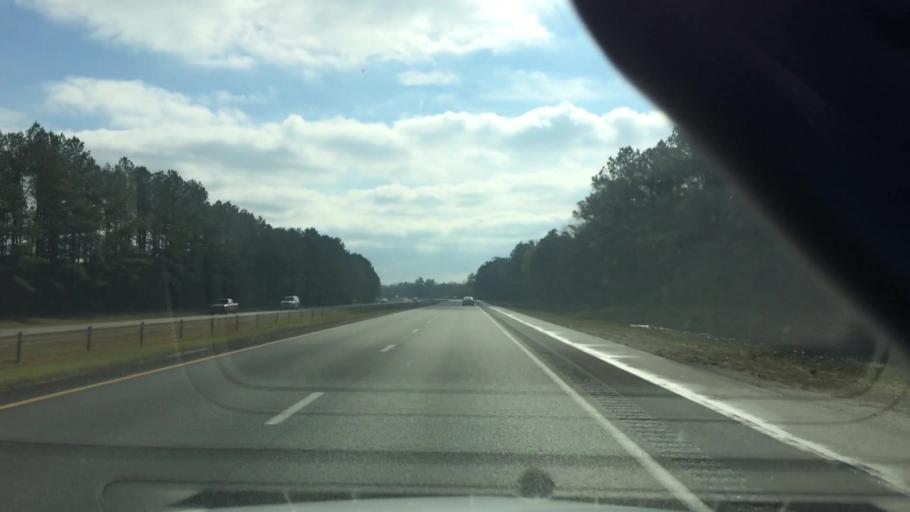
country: US
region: North Carolina
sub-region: Pender County
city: Rocky Point
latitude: 34.4701
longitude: -77.8799
